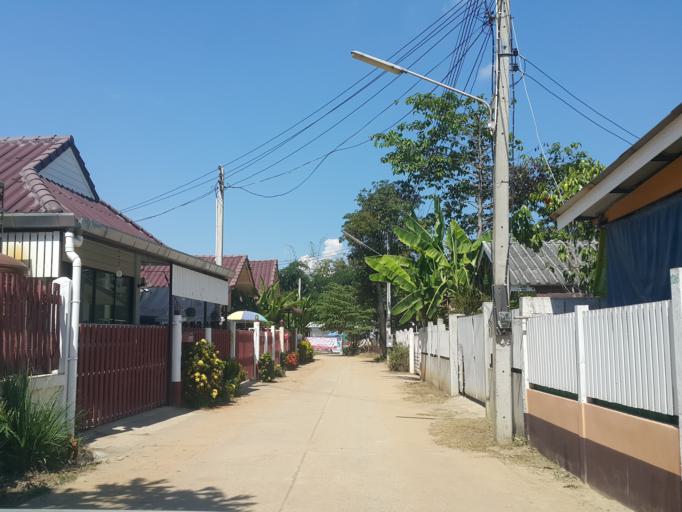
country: TH
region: Chiang Mai
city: Saraphi
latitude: 18.7664
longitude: 99.0494
